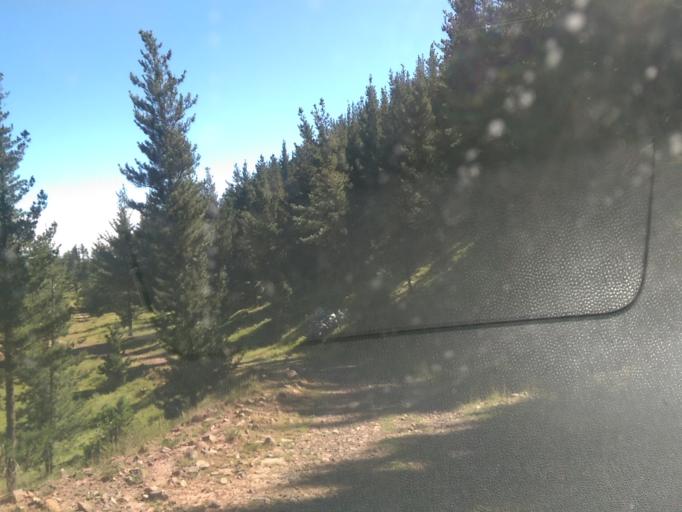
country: LS
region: Maseru
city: Maseru
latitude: -29.4916
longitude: 27.5819
